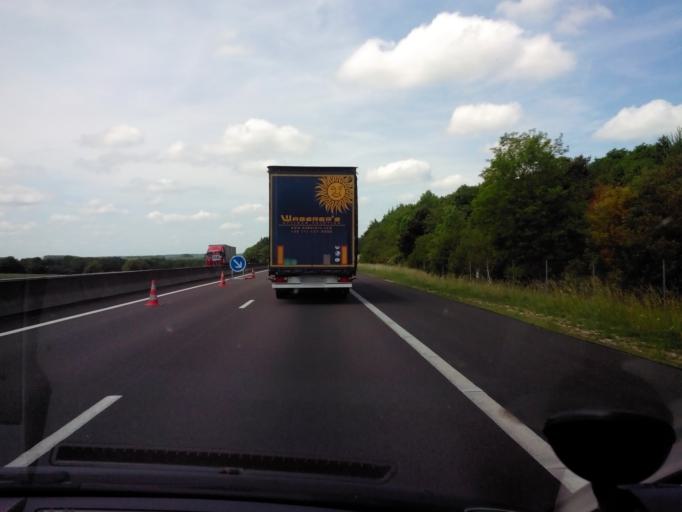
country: FR
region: Champagne-Ardenne
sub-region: Departement de la Haute-Marne
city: Rolampont
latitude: 47.9193
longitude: 5.2411
